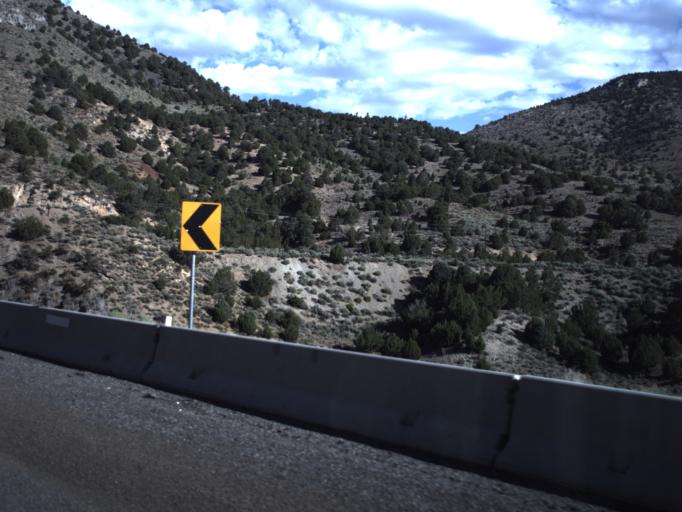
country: US
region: Utah
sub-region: Utah County
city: Genola
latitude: 39.9753
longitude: -112.0687
